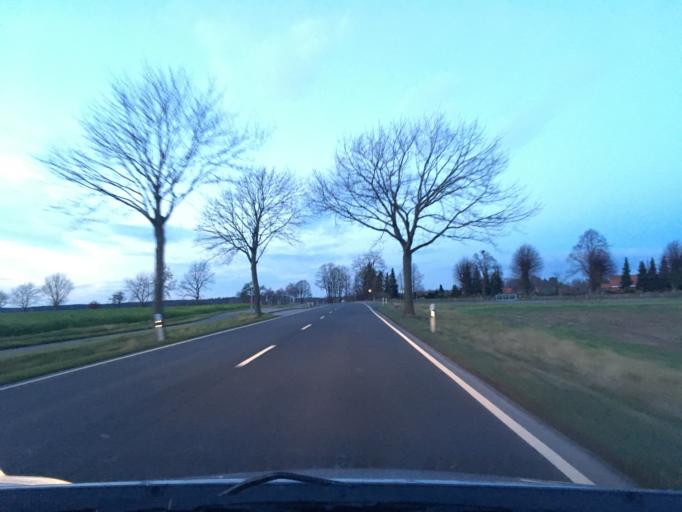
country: DE
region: Lower Saxony
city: Luechow
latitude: 52.9833
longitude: 11.1267
